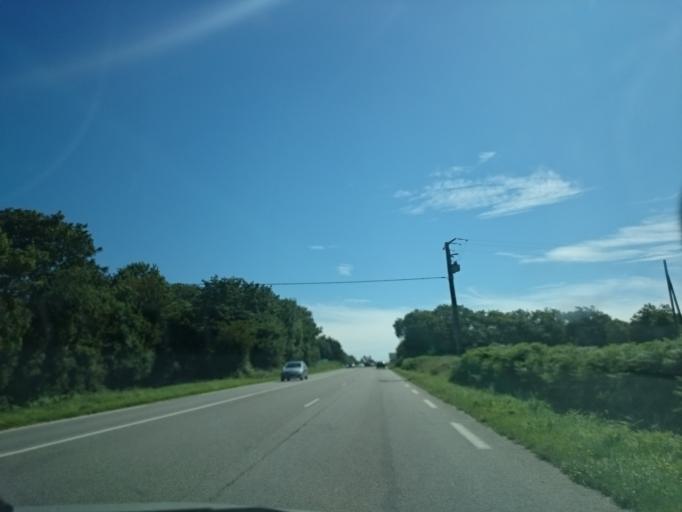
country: FR
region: Brittany
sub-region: Departement du Finistere
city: Guilers
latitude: 48.4278
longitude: -4.5825
